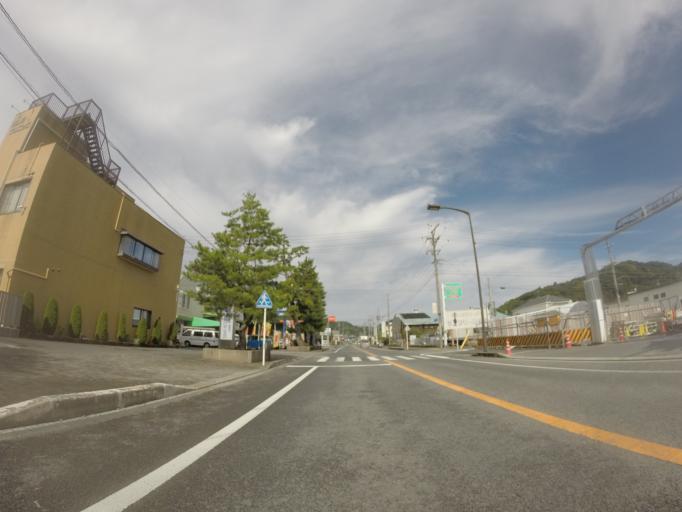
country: JP
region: Shizuoka
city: Fujieda
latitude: 34.9065
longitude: 138.2823
